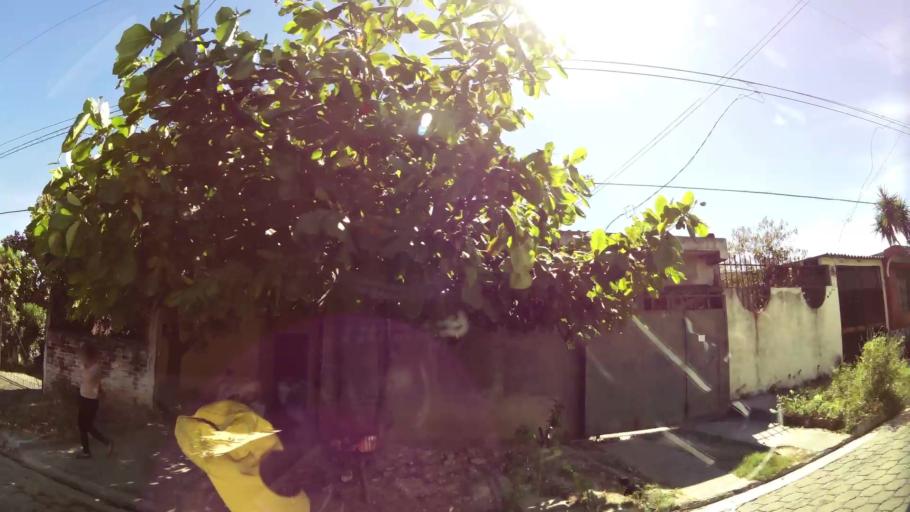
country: SV
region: San Salvador
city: Apopa
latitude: 13.8108
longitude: -89.1768
